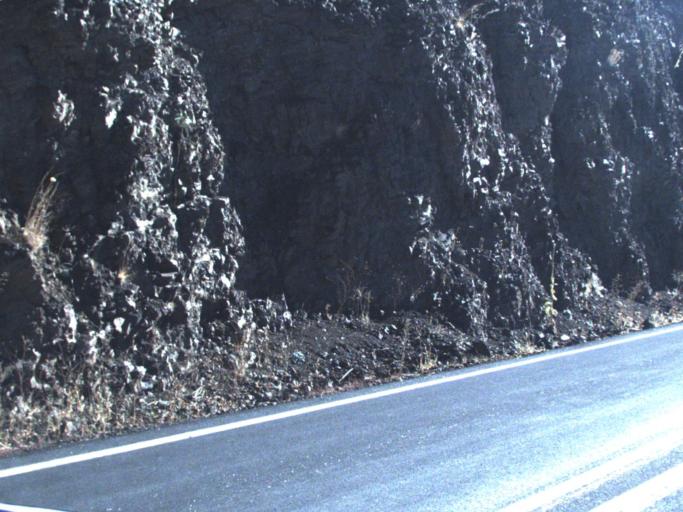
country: US
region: Washington
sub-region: Asotin County
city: Asotin
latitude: 46.0724
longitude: -117.2094
